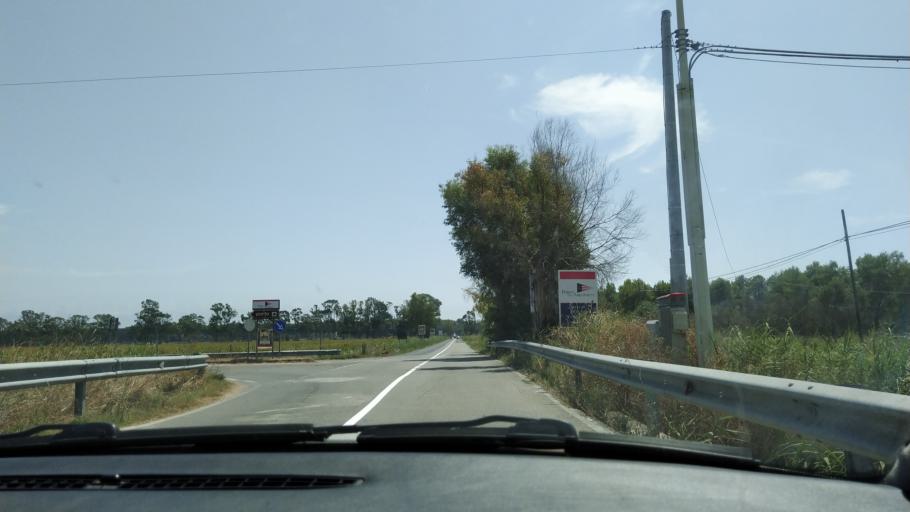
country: IT
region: Basilicate
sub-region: Provincia di Matera
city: Marconia
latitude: 40.3277
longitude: 16.7872
